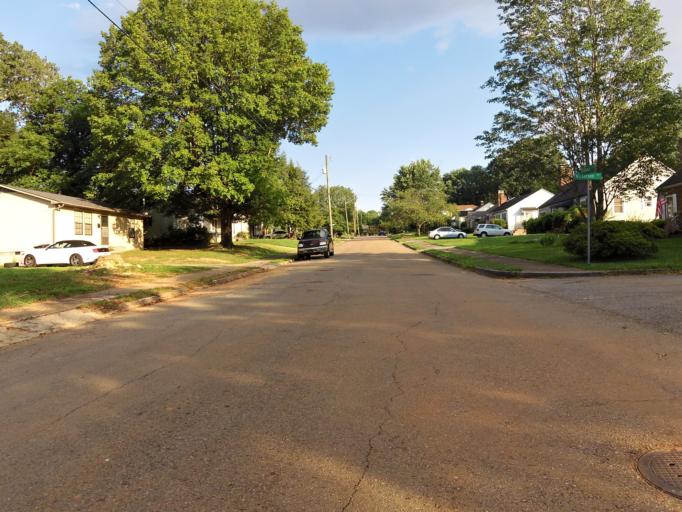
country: US
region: Tennessee
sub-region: Knox County
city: Knoxville
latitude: 36.0054
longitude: -83.9158
